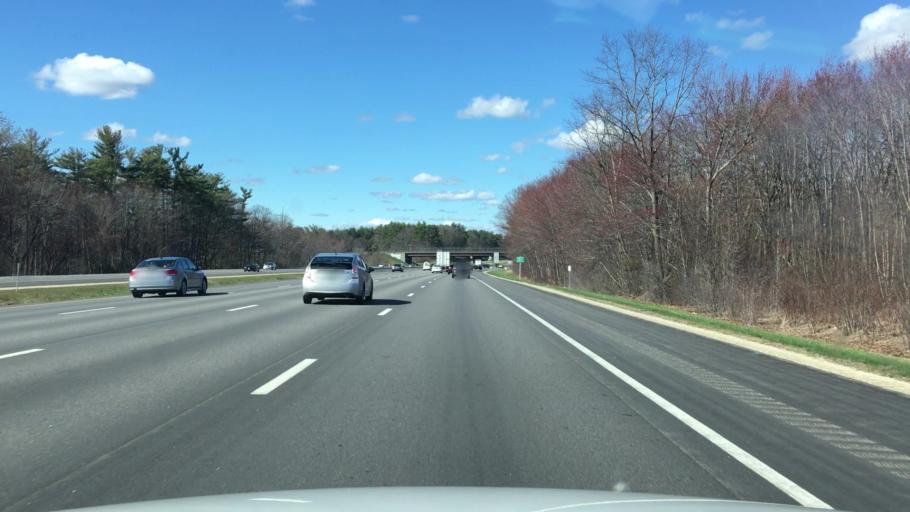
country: US
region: New Hampshire
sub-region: Rockingham County
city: Seabrook
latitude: 42.9024
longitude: -70.8779
